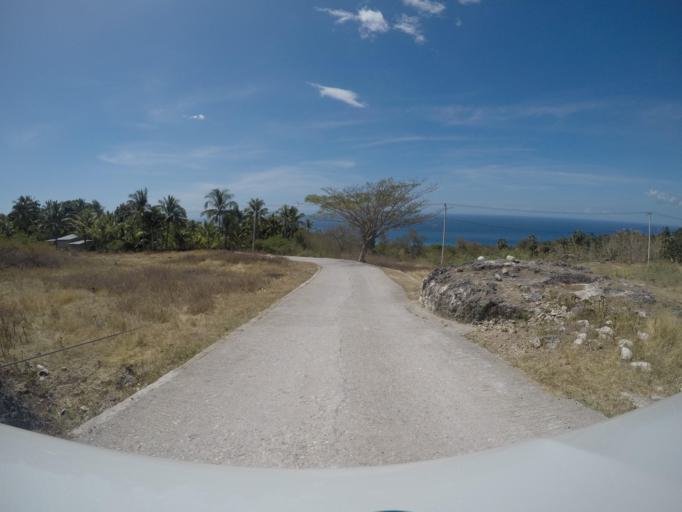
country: TL
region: Baucau
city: Baucau
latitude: -8.4514
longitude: 126.4487
